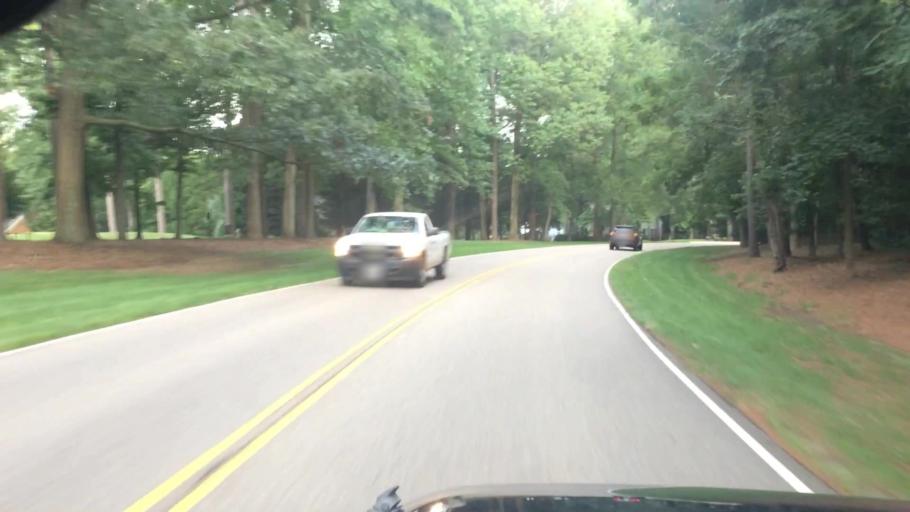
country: US
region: Virginia
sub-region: City of Williamsburg
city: Williamsburg
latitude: 37.2329
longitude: -76.6775
